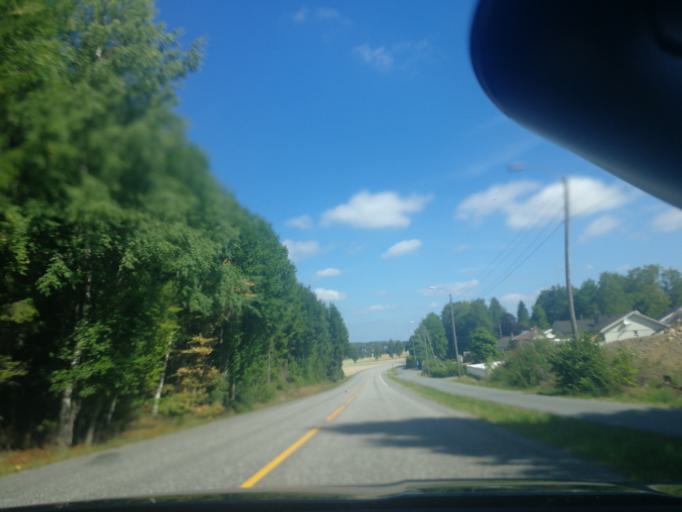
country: NO
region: Vestfold
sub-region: Sandefjord
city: Sandefjord
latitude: 59.1835
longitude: 10.2166
